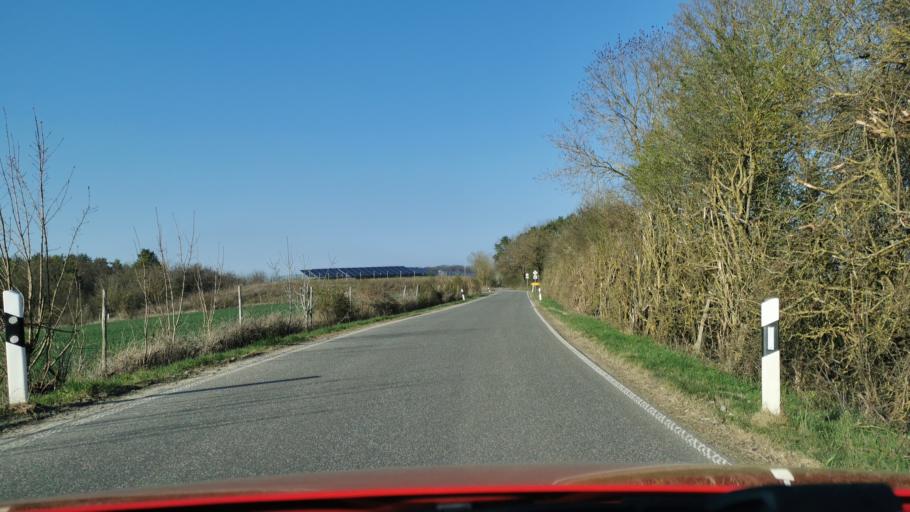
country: DE
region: Rheinland-Pfalz
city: Trierweiler
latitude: 49.7871
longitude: 6.5545
